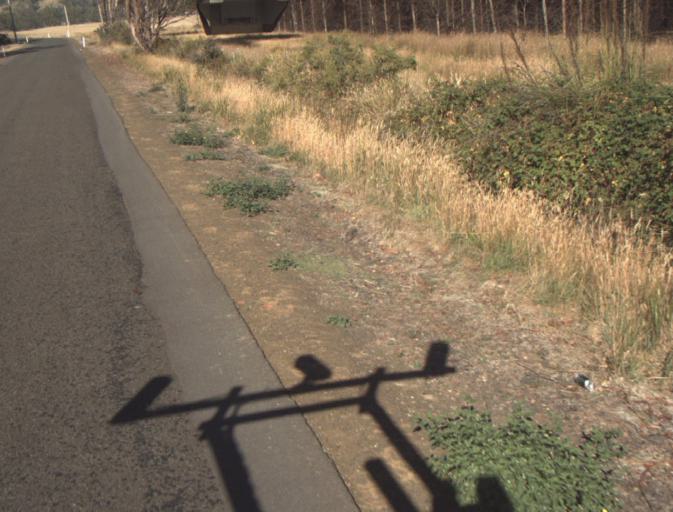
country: AU
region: Tasmania
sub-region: Launceston
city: Newstead
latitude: -41.3271
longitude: 147.3137
